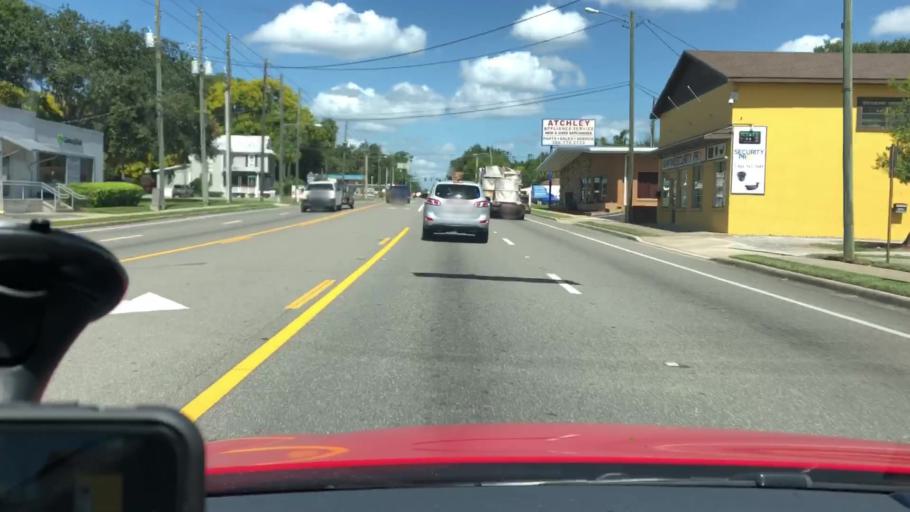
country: US
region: Florida
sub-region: Volusia County
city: Orange City
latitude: 28.9497
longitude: -81.2988
